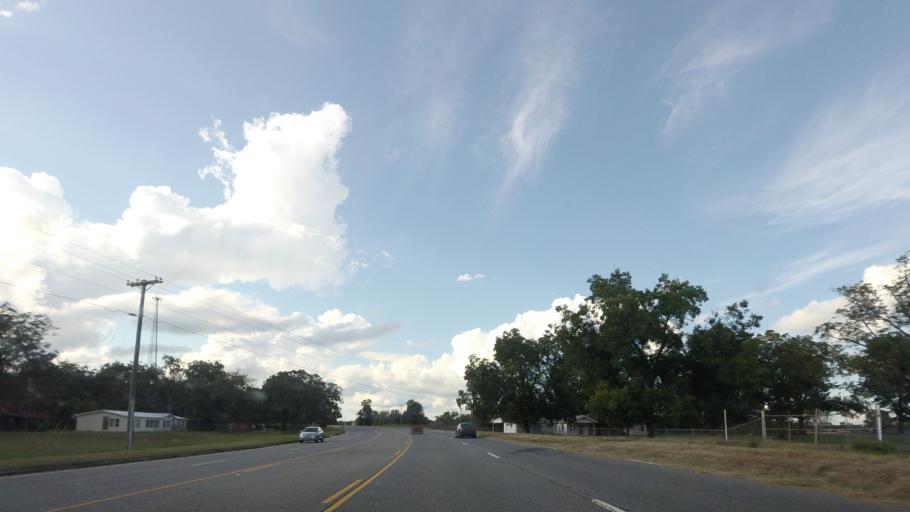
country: US
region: Georgia
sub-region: Houston County
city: Perry
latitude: 32.3891
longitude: -83.6221
